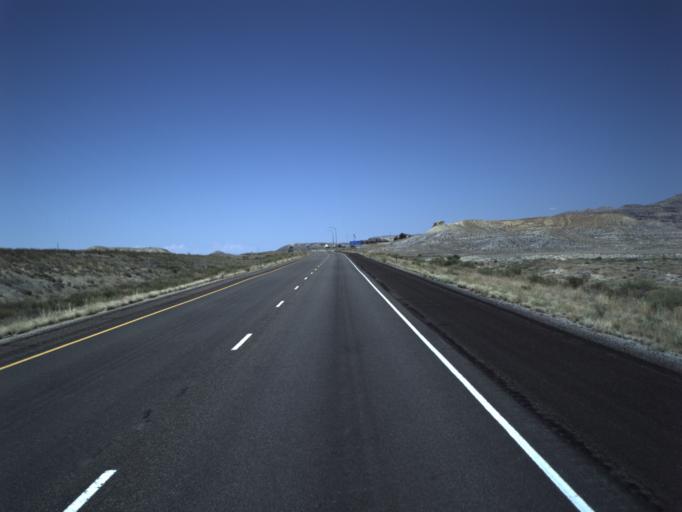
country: US
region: Utah
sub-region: Grand County
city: Moab
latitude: 38.9495
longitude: -109.6733
